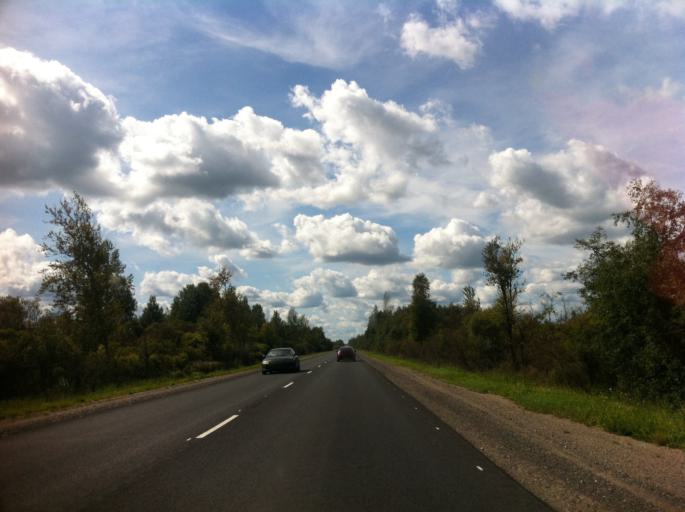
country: RU
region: Pskov
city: Izborsk
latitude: 57.7448
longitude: 28.0276
